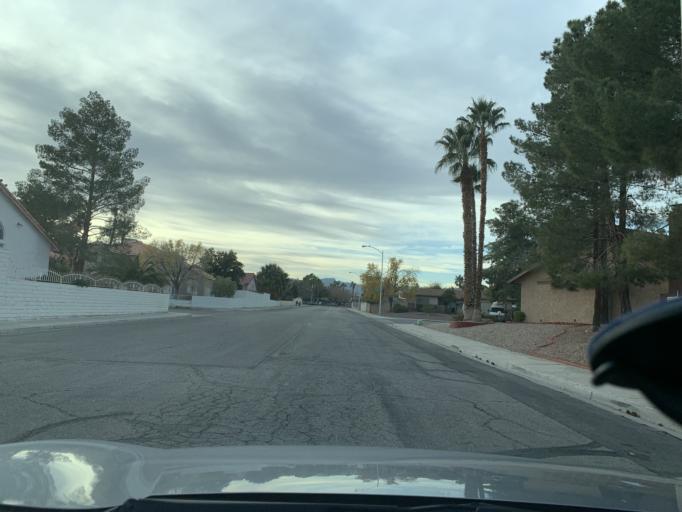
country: US
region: Nevada
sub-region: Clark County
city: Spring Valley
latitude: 36.0971
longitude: -115.2317
